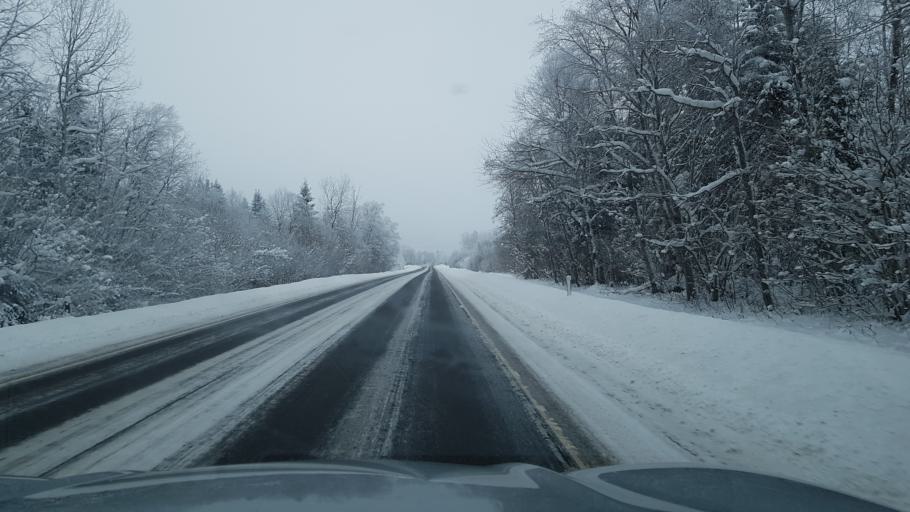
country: EE
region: Ida-Virumaa
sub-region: Johvi vald
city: Johvi
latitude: 59.2802
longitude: 27.3931
